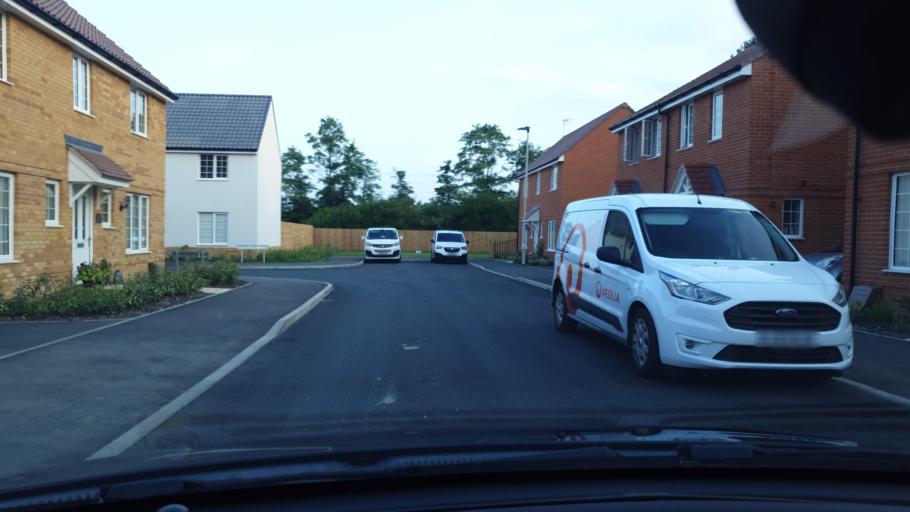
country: GB
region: England
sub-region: Essex
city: Frinton-on-Sea
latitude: 51.8434
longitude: 1.2040
